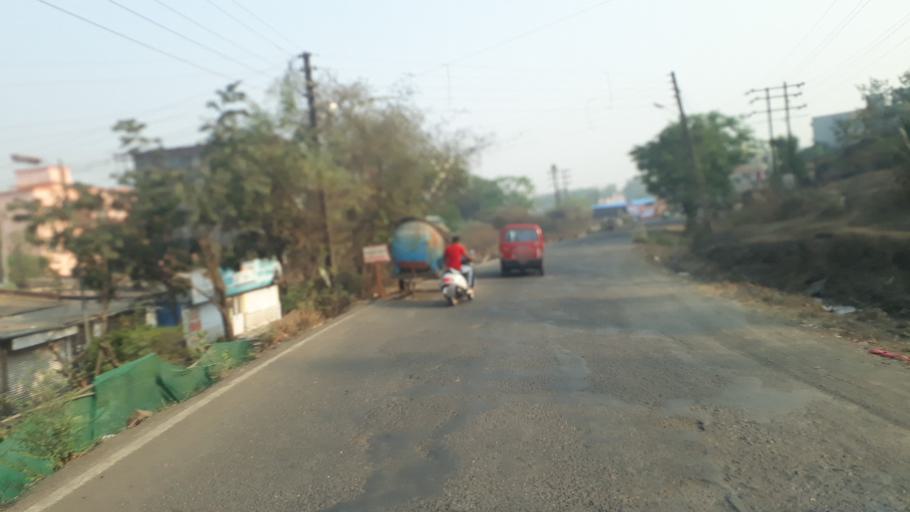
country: IN
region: Maharashtra
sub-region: Raigarh
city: Neral
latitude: 19.0202
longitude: 73.3116
